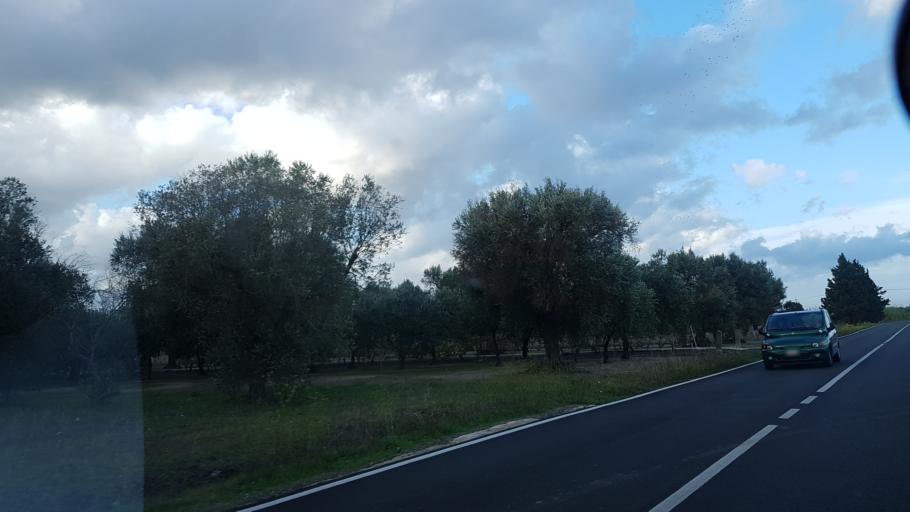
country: IT
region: Apulia
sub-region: Provincia di Brindisi
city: San Pietro Vernotico
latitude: 40.5094
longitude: 18.0090
